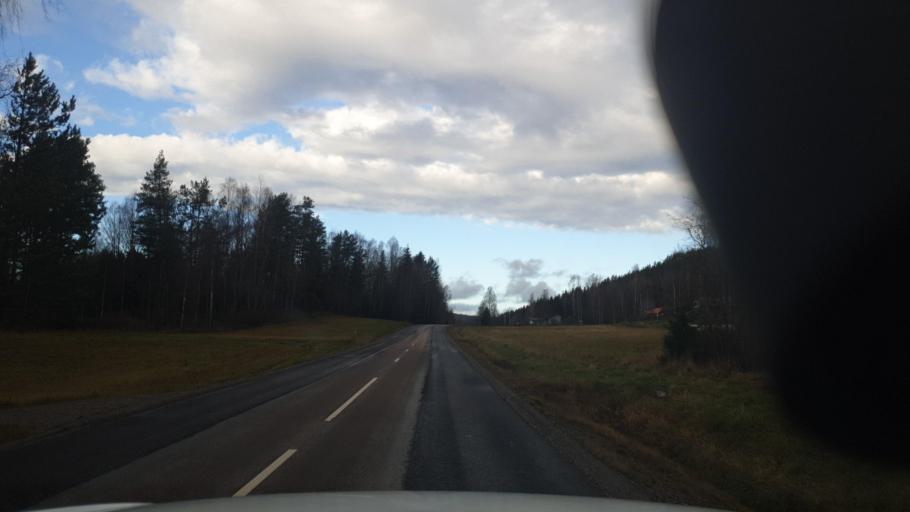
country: SE
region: Vaermland
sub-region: Arvika Kommun
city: Arvika
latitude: 59.8006
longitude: 12.6052
